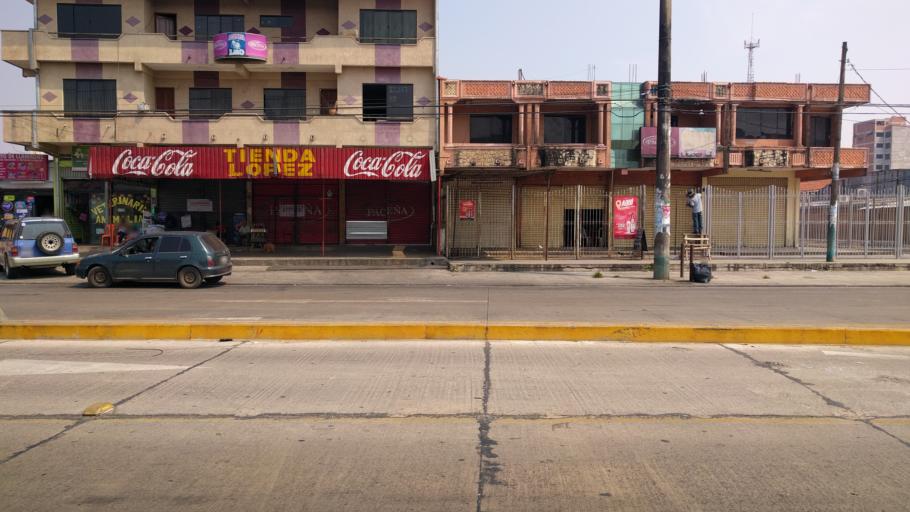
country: BO
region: Santa Cruz
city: Santa Cruz de la Sierra
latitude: -17.7796
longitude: -63.2037
